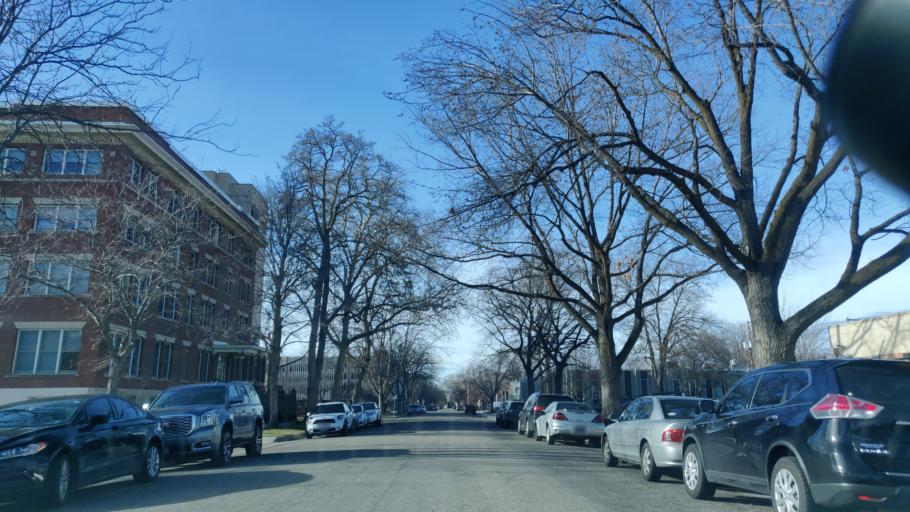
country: US
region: Idaho
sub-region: Ada County
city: Boise
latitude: 43.6168
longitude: -116.1943
